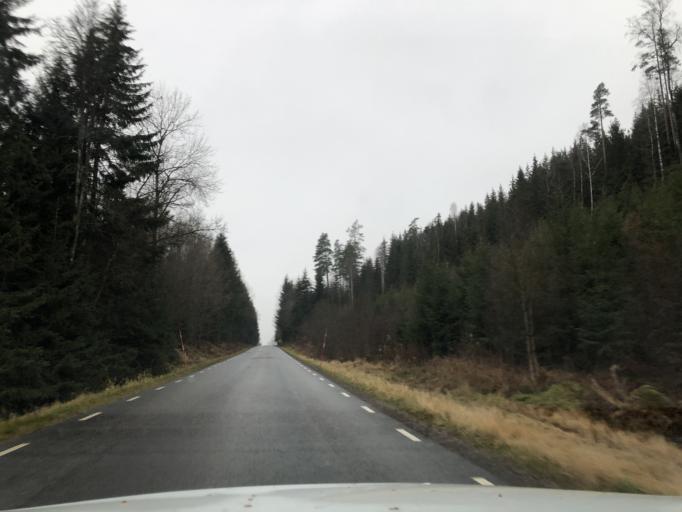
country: SE
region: Vaestra Goetaland
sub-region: Ulricehamns Kommun
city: Ulricehamn
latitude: 57.8325
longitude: 13.3997
